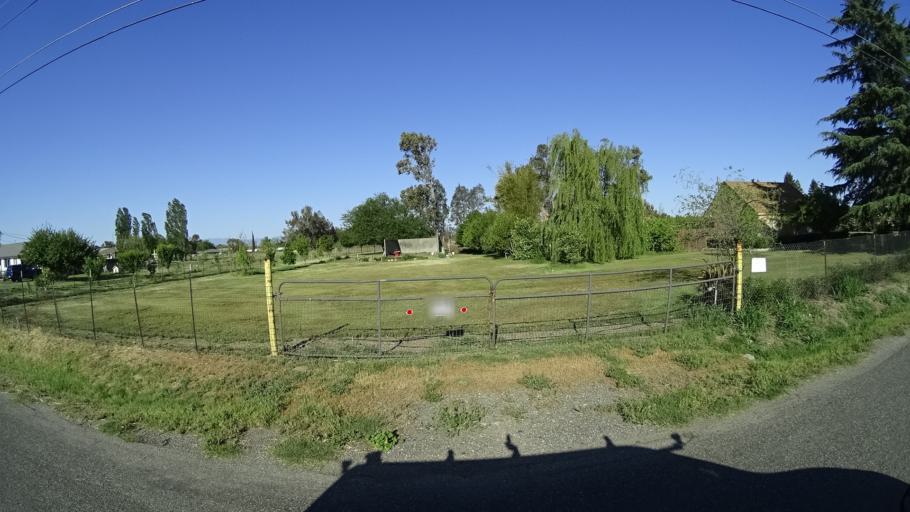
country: US
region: California
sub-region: Glenn County
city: Orland
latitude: 39.7313
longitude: -122.1874
